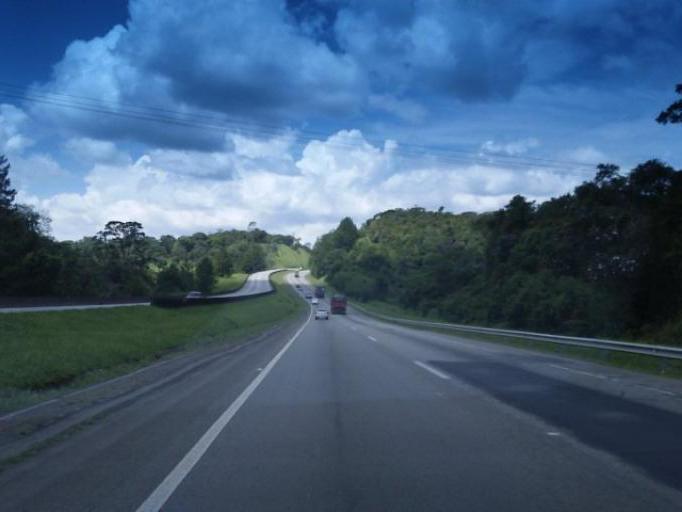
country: BR
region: Sao Paulo
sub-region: Juquitiba
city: Juquitiba
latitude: -23.9608
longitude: -47.1200
